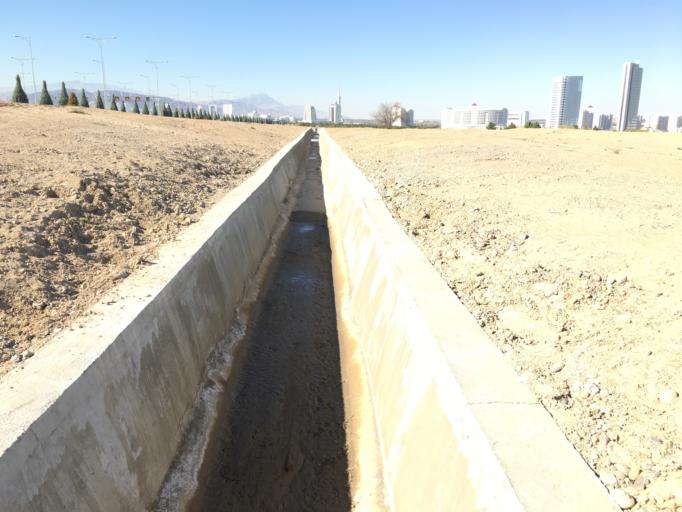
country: TM
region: Ahal
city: Ashgabat
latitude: 37.8826
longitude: 58.3491
